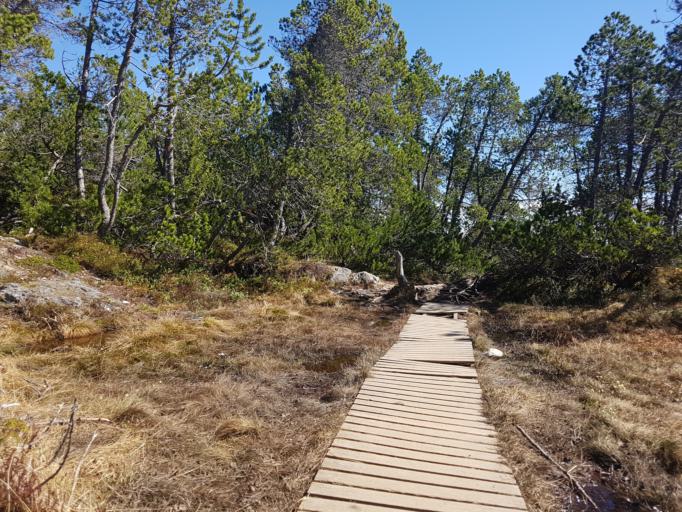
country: NO
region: Sor-Trondelag
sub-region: Trondheim
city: Trondheim
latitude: 63.4330
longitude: 10.3063
